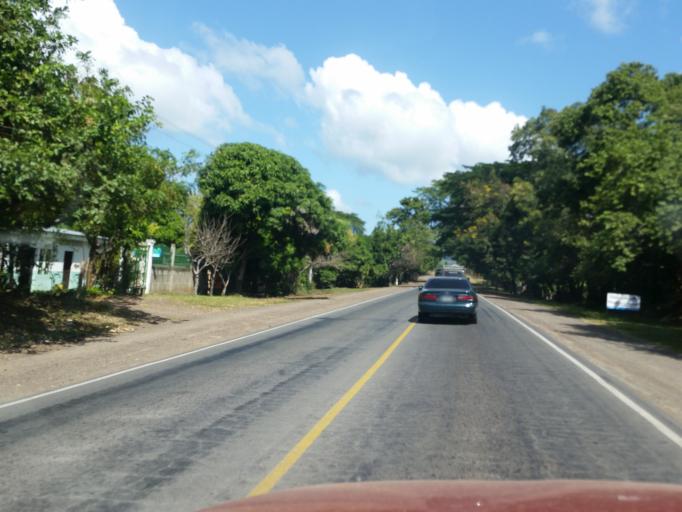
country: NI
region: Granada
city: Diriomo
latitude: 11.8372
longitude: -86.0307
